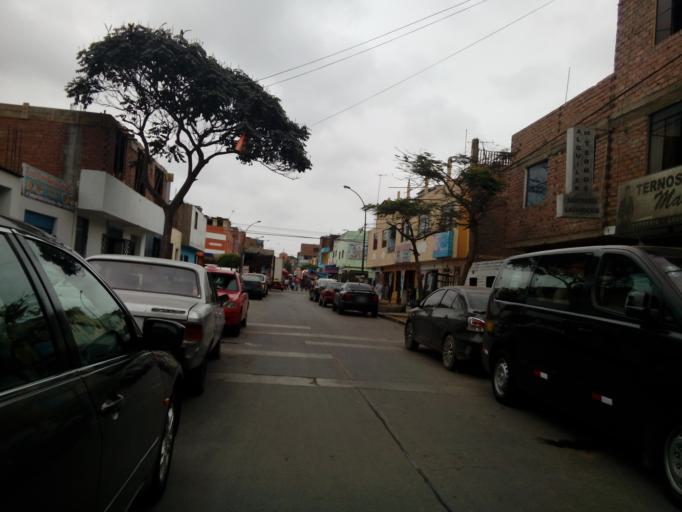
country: PE
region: Callao
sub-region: Callao
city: Callao
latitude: -12.0408
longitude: -77.0963
